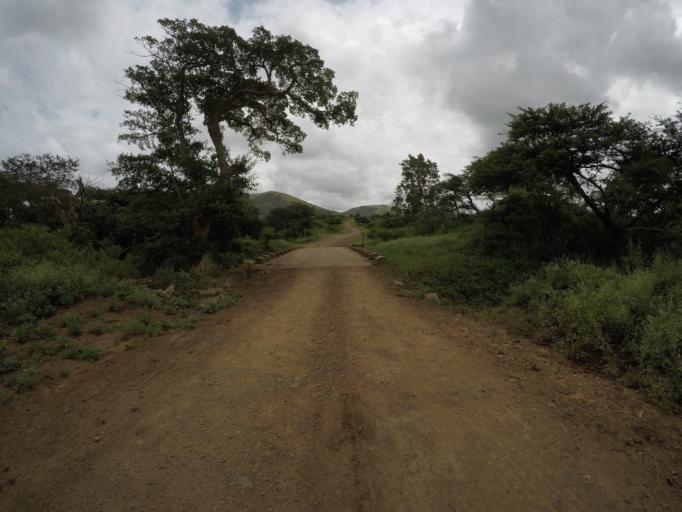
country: ZA
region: KwaZulu-Natal
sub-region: uThungulu District Municipality
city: Empangeni
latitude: -28.5963
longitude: 31.8915
